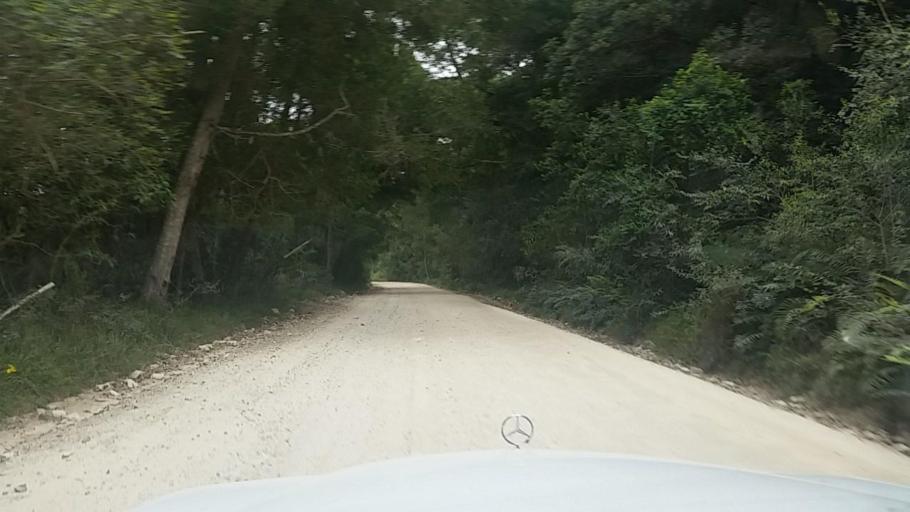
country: ZA
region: Western Cape
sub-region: Eden District Municipality
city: Knysna
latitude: -33.9773
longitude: 23.1387
